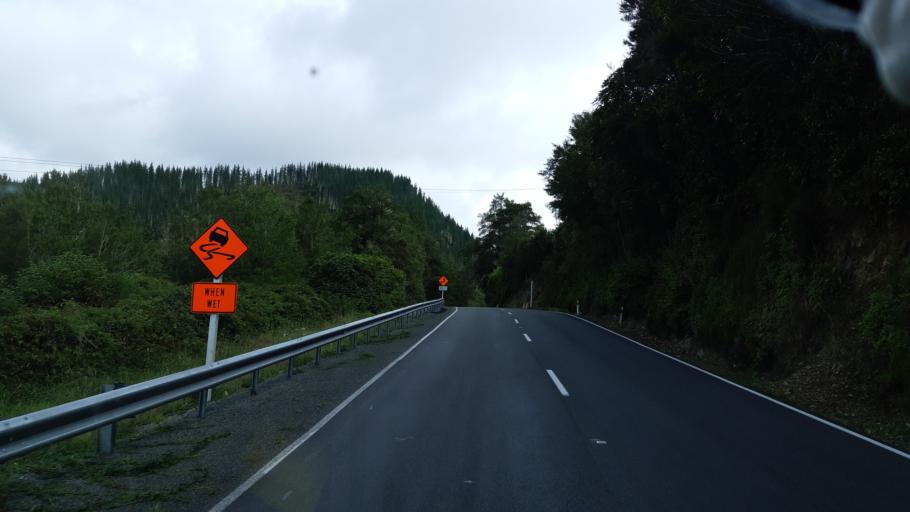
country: NZ
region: West Coast
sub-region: Buller District
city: Westport
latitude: -41.9647
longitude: 172.2030
